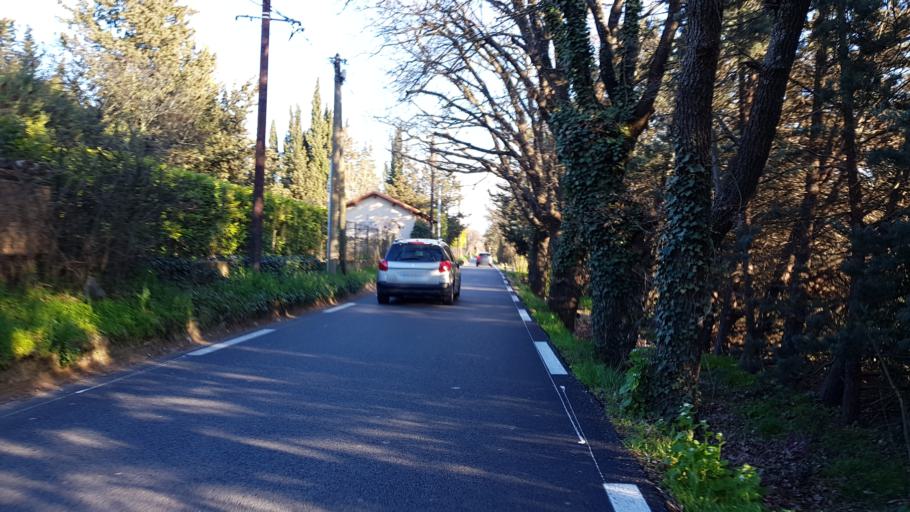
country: FR
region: Provence-Alpes-Cote d'Azur
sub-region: Departement des Bouches-du-Rhone
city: Bouc-Bel-Air
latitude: 43.4942
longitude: 5.4109
